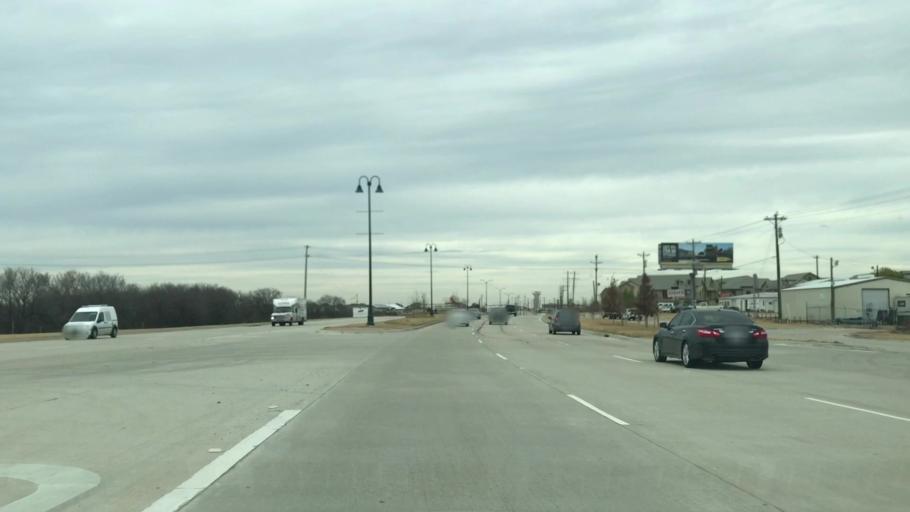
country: US
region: Texas
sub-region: Denton County
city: The Colony
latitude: 33.1182
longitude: -96.8920
